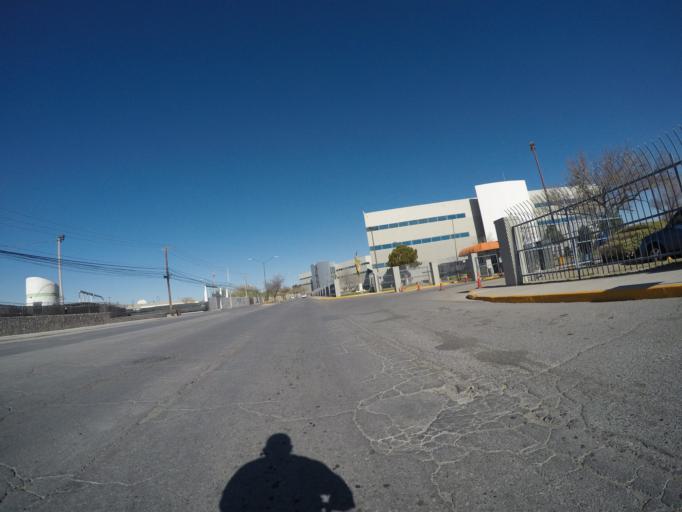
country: MX
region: Chihuahua
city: Ciudad Juarez
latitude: 31.7485
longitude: -106.4369
